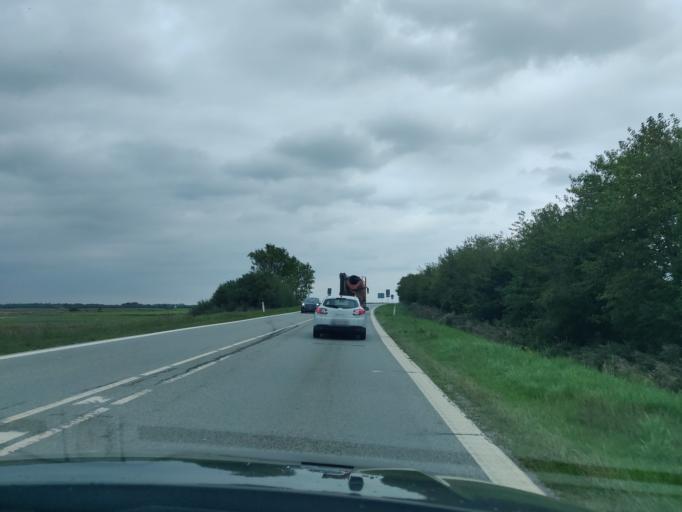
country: DK
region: North Denmark
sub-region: Alborg Kommune
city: Frejlev
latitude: 57.0103
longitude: 9.7394
